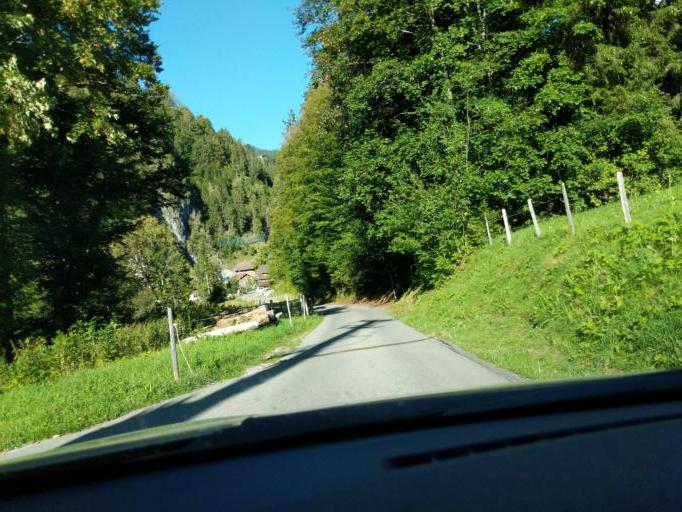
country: CH
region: Bern
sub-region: Obersimmental-Saanen District
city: Zweisimmen
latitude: 46.6092
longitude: 7.2826
